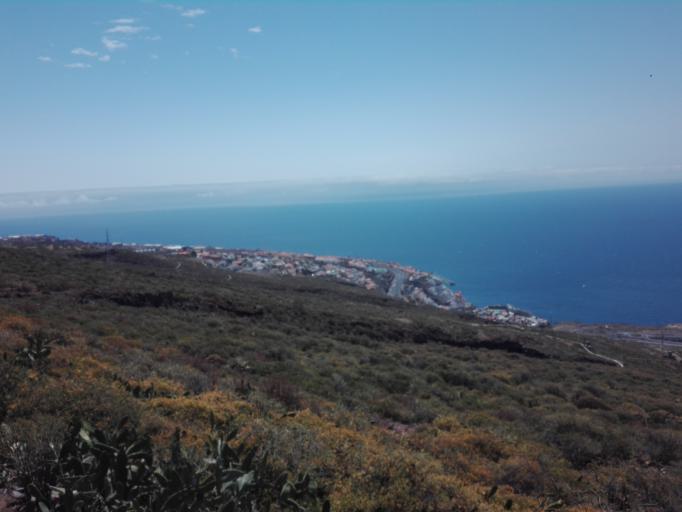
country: ES
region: Canary Islands
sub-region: Provincia de Santa Cruz de Tenerife
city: Candelaria
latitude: 28.4109
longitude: -16.3485
